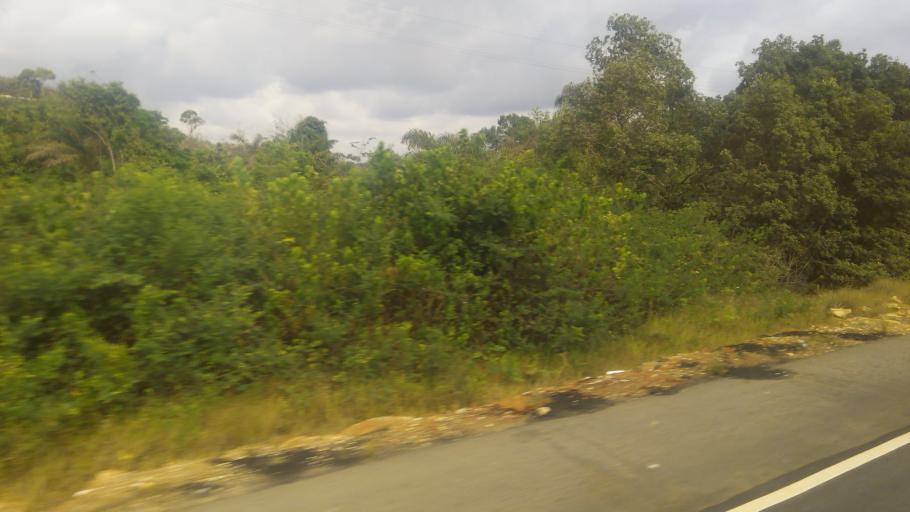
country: GH
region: Western
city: Axim
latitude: 4.9012
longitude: -2.2670
